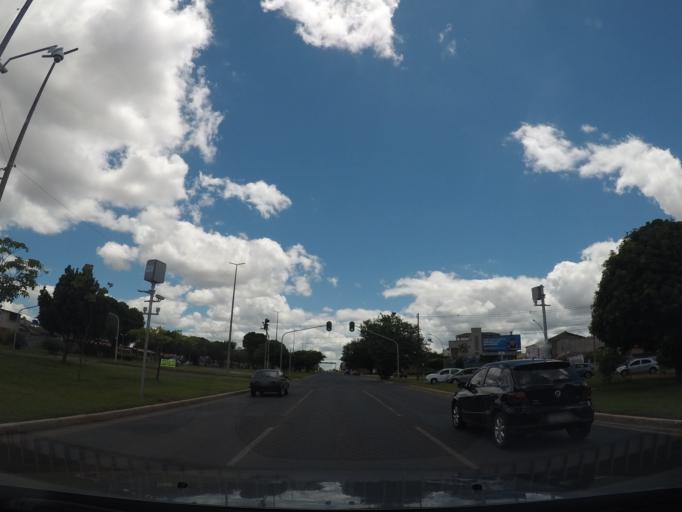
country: BR
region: Federal District
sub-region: Brasilia
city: Brasilia
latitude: -15.8467
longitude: -47.9752
